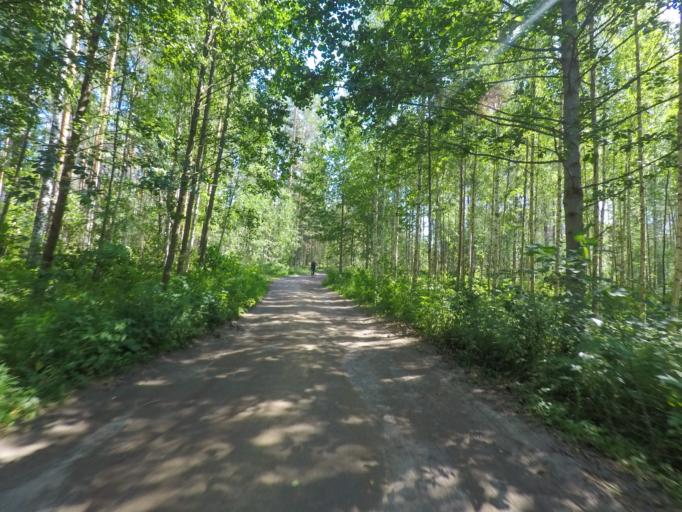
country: FI
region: Southern Savonia
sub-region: Mikkeli
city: Puumala
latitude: 61.4304
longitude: 28.0042
